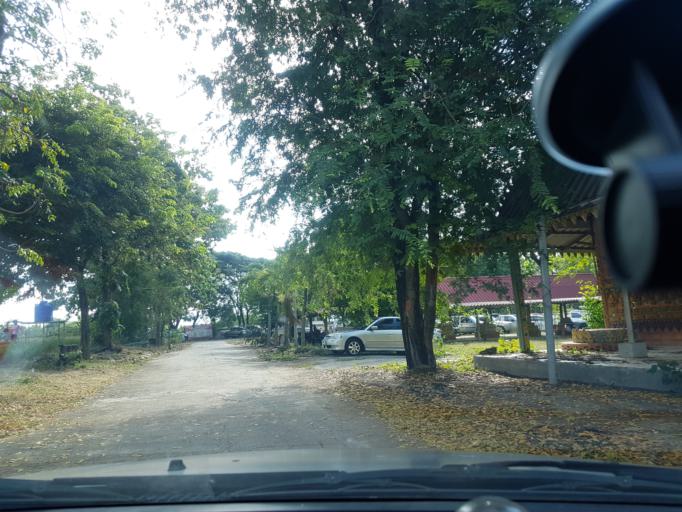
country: TH
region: Lop Buri
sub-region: Amphoe Tha Luang
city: Tha Luang
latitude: 15.0654
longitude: 101.0510
